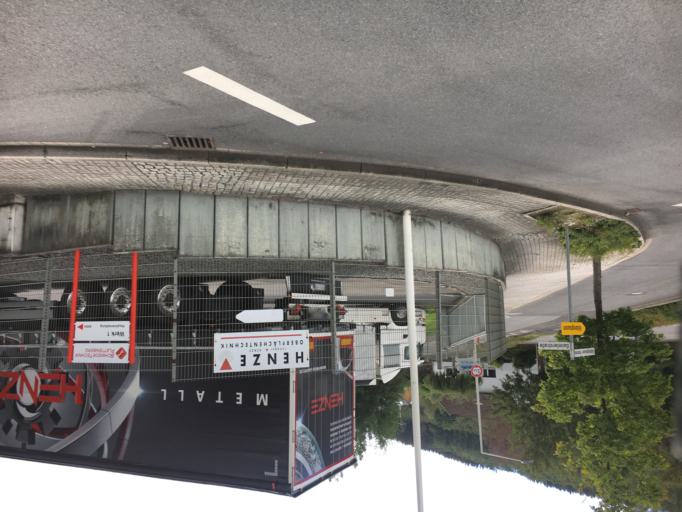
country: DE
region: North Rhine-Westphalia
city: Plettenberg
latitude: 51.1971
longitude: 7.8320
